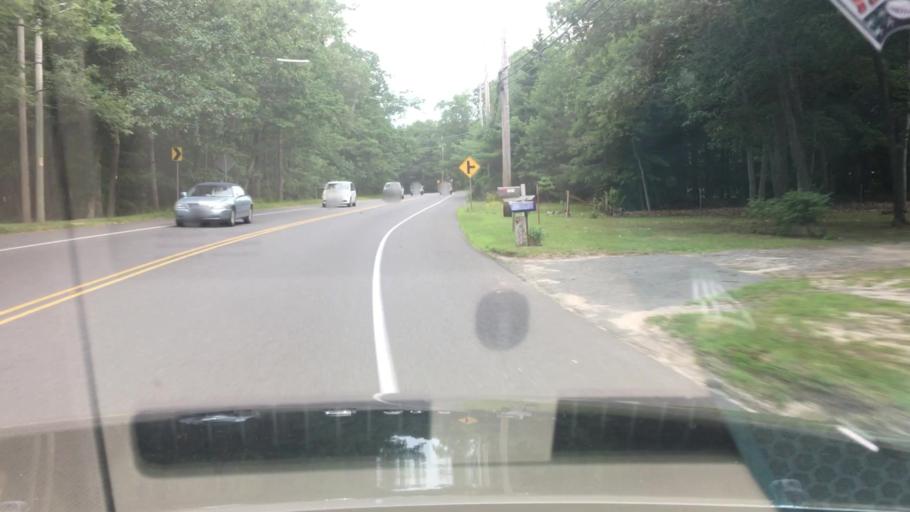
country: US
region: New Jersey
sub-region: Ocean County
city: Cedar Glen West
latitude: 40.0424
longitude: -74.3142
